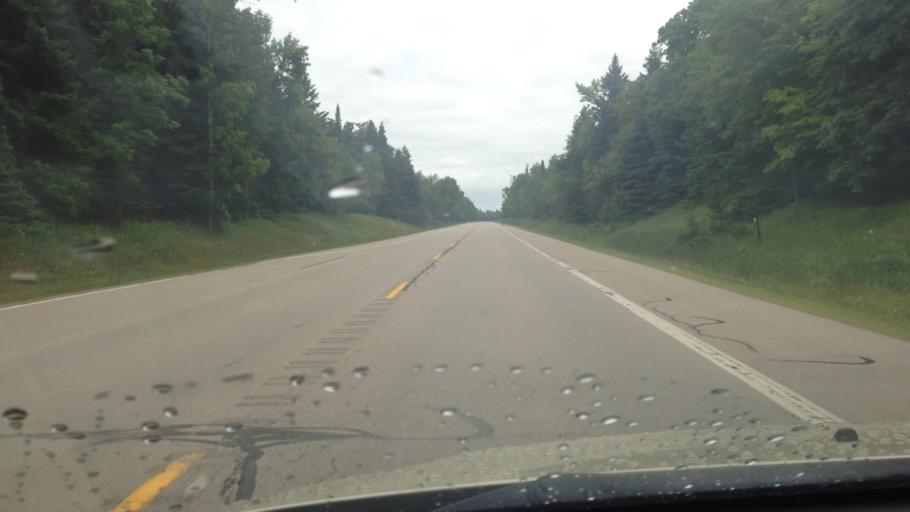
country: US
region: Michigan
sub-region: Menominee County
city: Menominee
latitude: 45.3960
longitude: -87.3671
